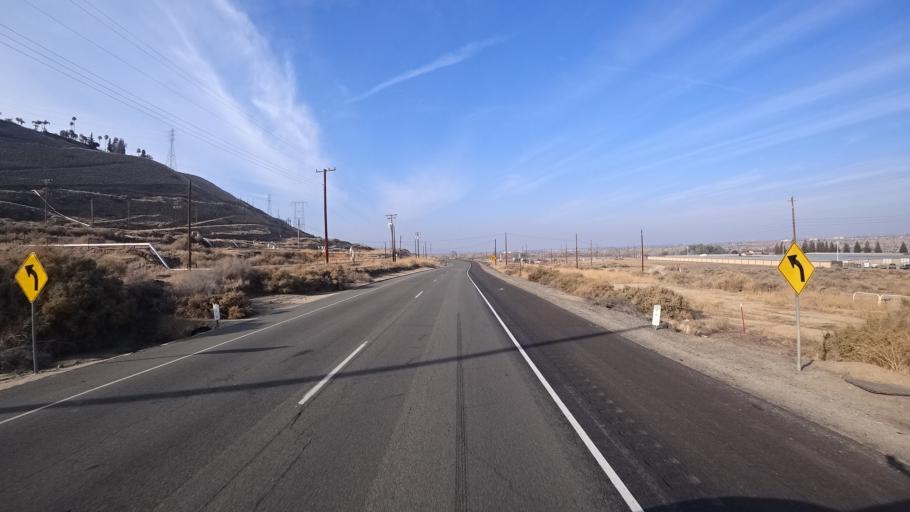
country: US
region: California
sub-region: Kern County
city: Oildale
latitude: 35.4164
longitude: -118.9635
